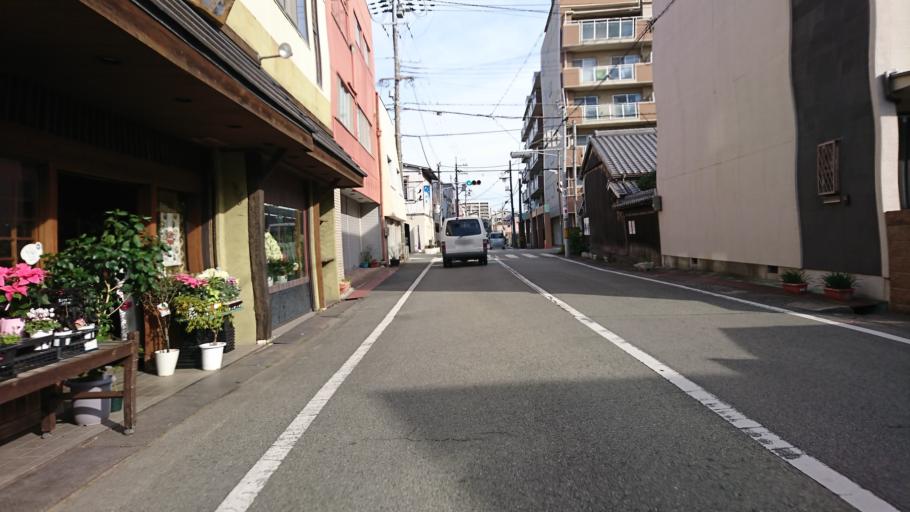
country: JP
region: Hyogo
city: Kakogawacho-honmachi
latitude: 34.7486
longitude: 134.8013
